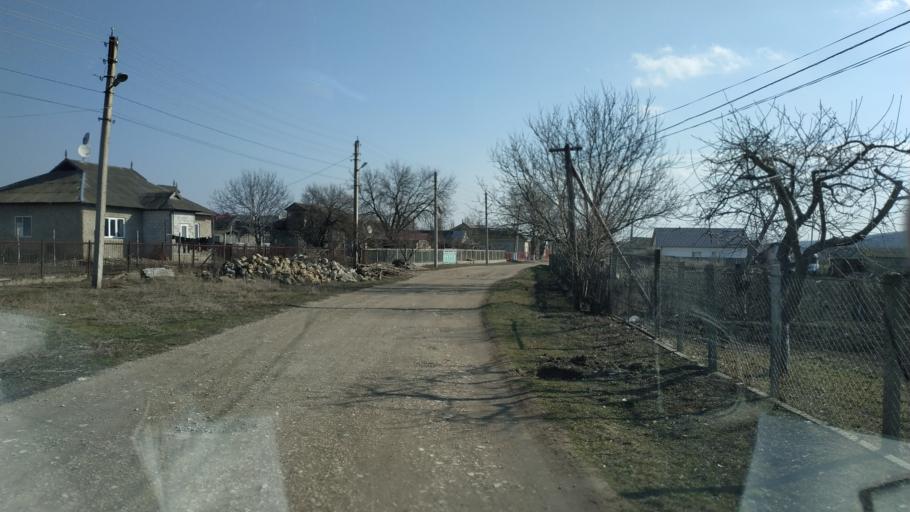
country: MD
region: Chisinau
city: Singera
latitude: 46.6821
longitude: 29.0499
